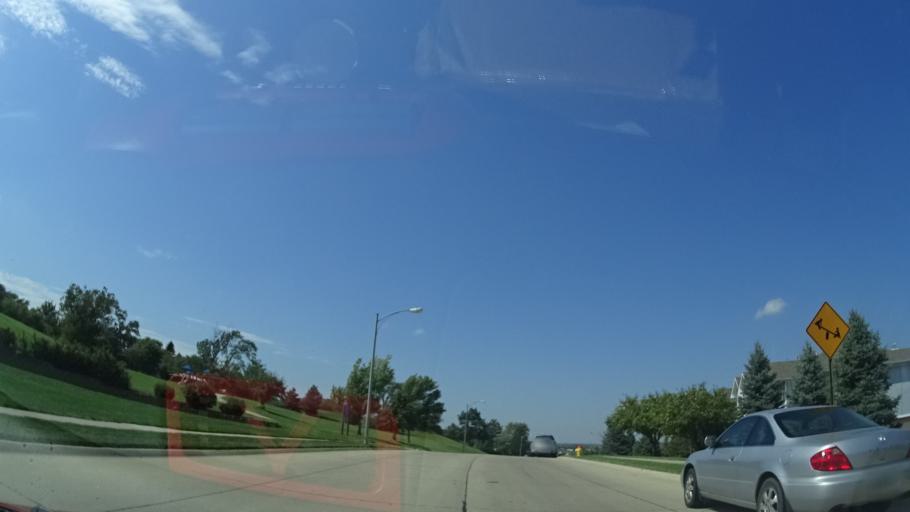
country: US
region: Nebraska
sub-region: Sarpy County
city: Offutt Air Force Base
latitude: 41.1357
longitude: -95.9552
